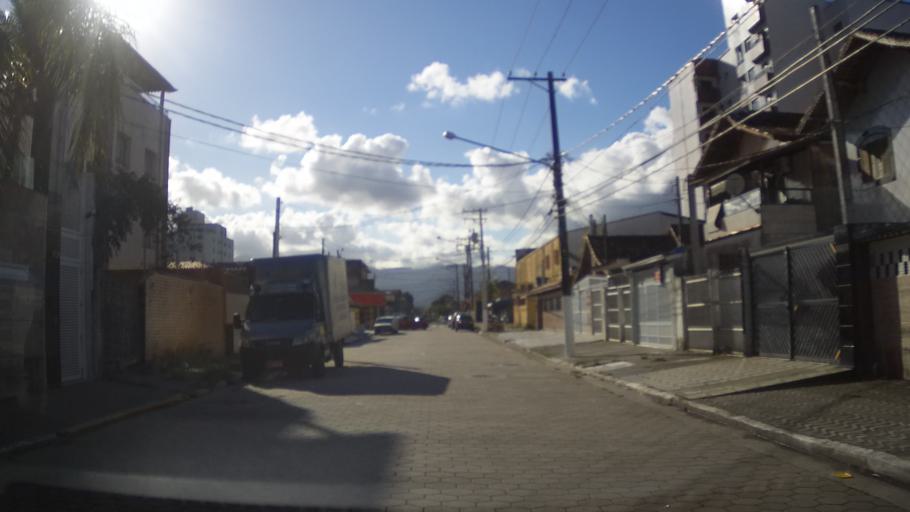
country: BR
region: Sao Paulo
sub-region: Praia Grande
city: Praia Grande
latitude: -24.0275
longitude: -46.4807
